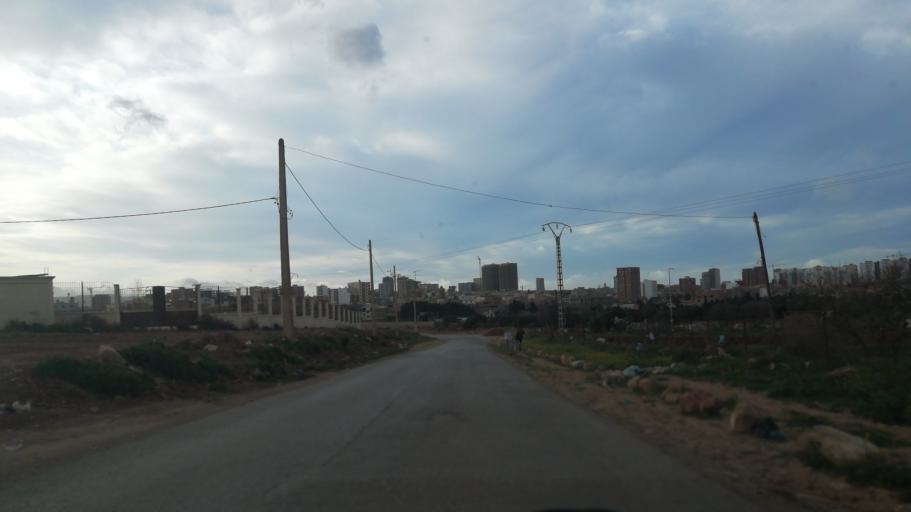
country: DZ
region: Oran
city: Bir el Djir
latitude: 35.7169
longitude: -0.5603
